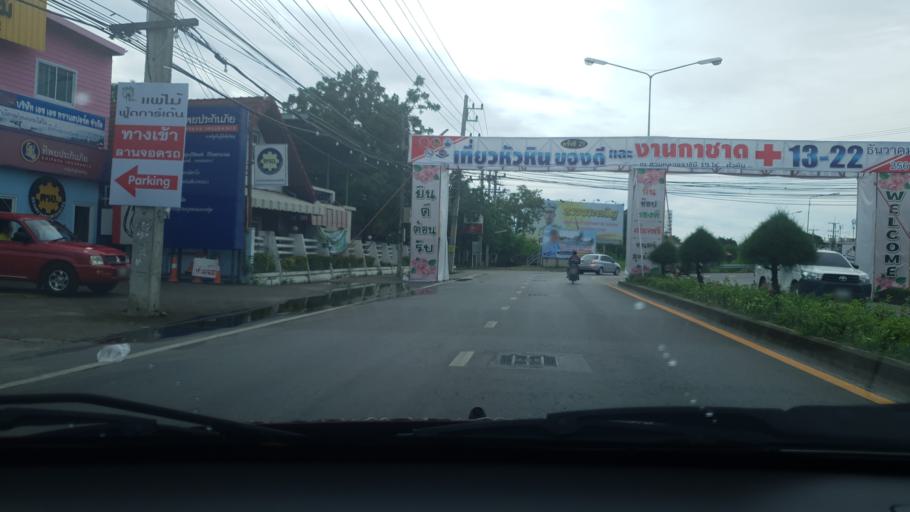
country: TH
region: Prachuap Khiri Khan
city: Hua Hin
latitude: 12.5749
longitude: 99.9510
